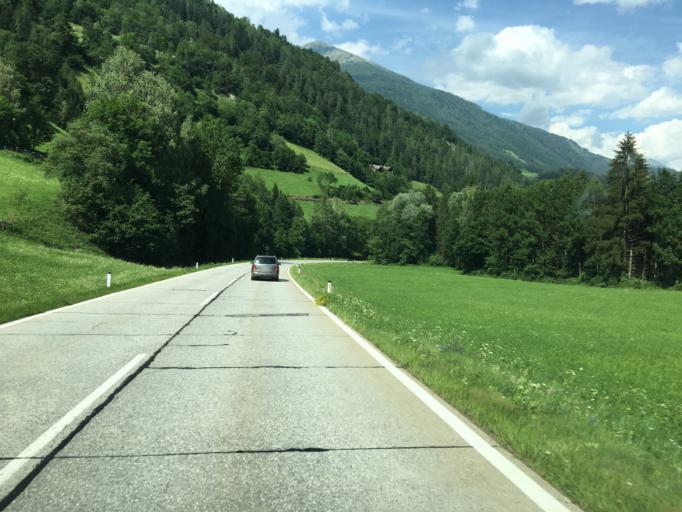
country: AT
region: Carinthia
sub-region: Politischer Bezirk Spittal an der Drau
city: Flattach
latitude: 46.9325
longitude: 13.0868
